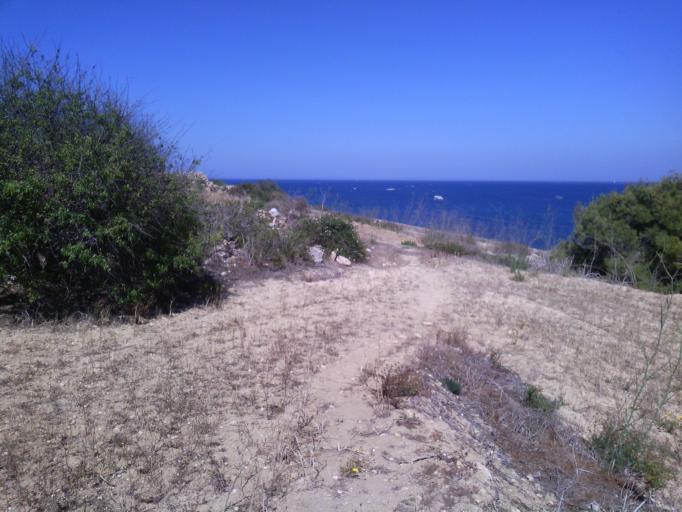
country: MT
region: Il-Mellieha
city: Mellieha
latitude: 35.9778
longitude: 14.3558
